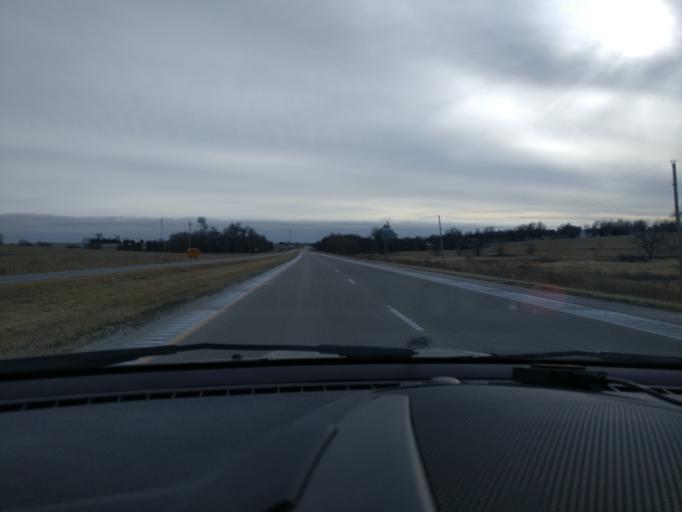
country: US
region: Nebraska
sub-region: Saunders County
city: Wahoo
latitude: 41.0686
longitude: -96.6404
